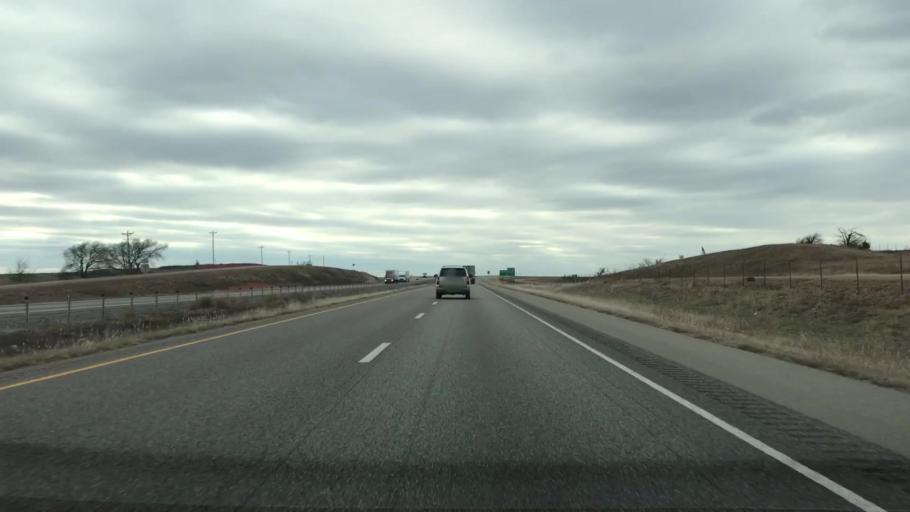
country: US
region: Oklahoma
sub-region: Beckham County
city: Sayre
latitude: 35.3425
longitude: -99.5860
